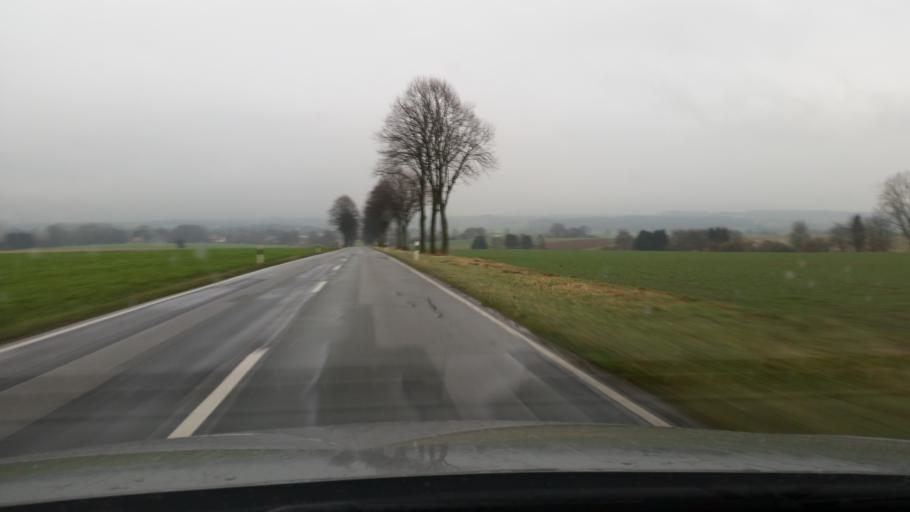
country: DE
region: Lower Saxony
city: Bad Munder am Deister
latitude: 52.1461
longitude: 9.4283
